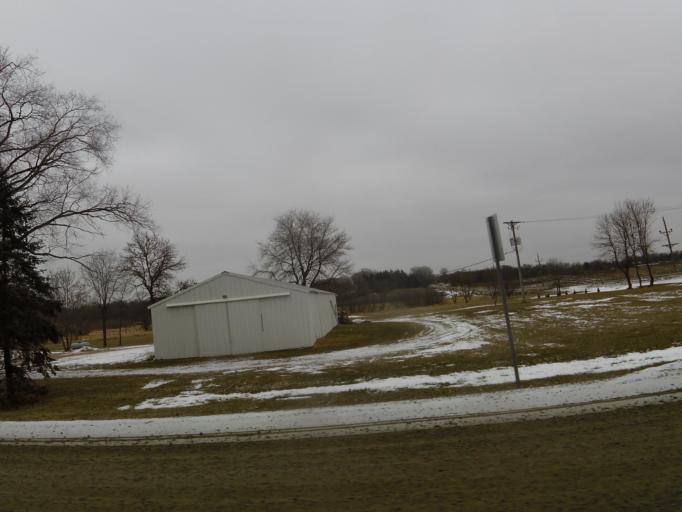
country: US
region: Minnesota
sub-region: Wright County
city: Montrose
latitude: 45.0362
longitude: -93.8583
